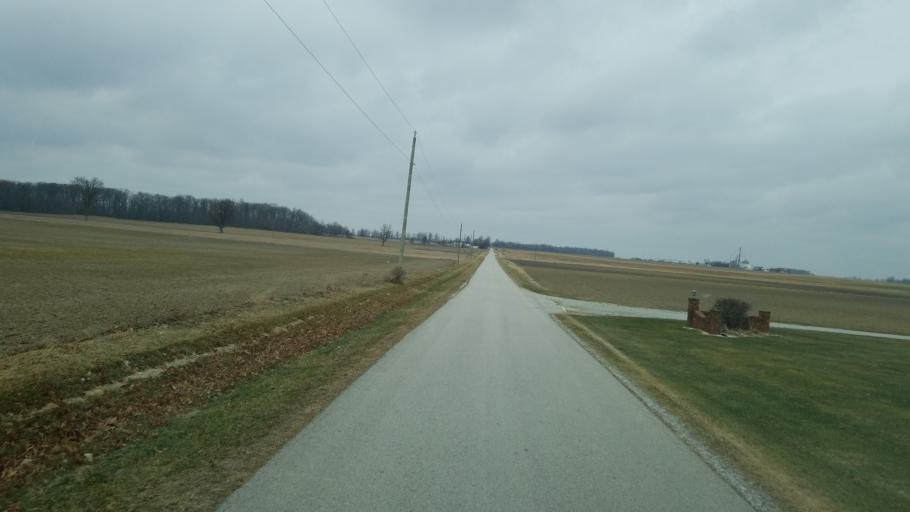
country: US
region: Ohio
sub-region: Hardin County
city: Forest
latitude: 40.7715
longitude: -83.4777
